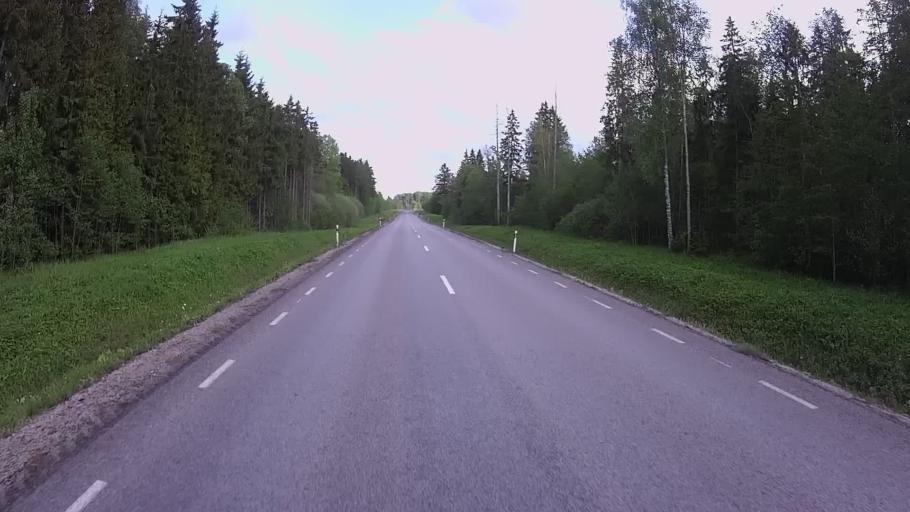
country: EE
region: Jogevamaa
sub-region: Mustvee linn
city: Mustvee
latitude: 59.0599
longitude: 27.0063
